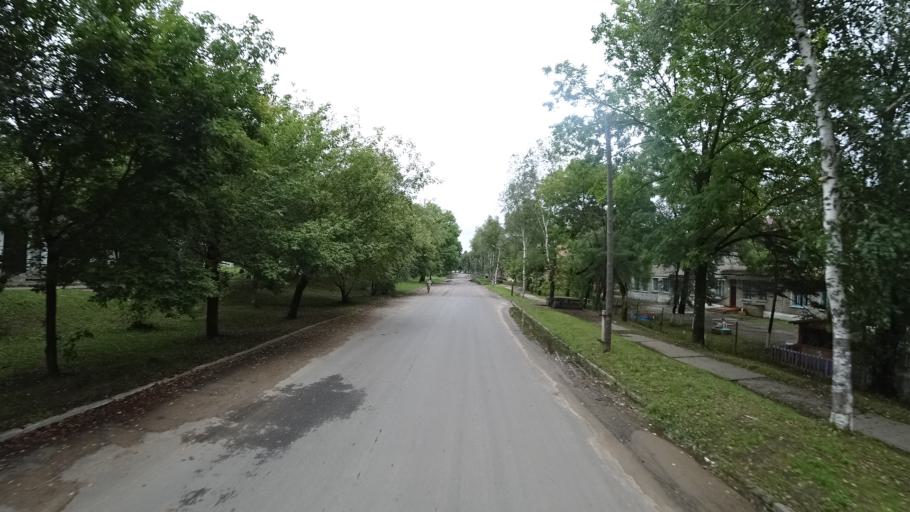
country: RU
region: Primorskiy
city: Rettikhovka
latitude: 44.1685
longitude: 132.7732
